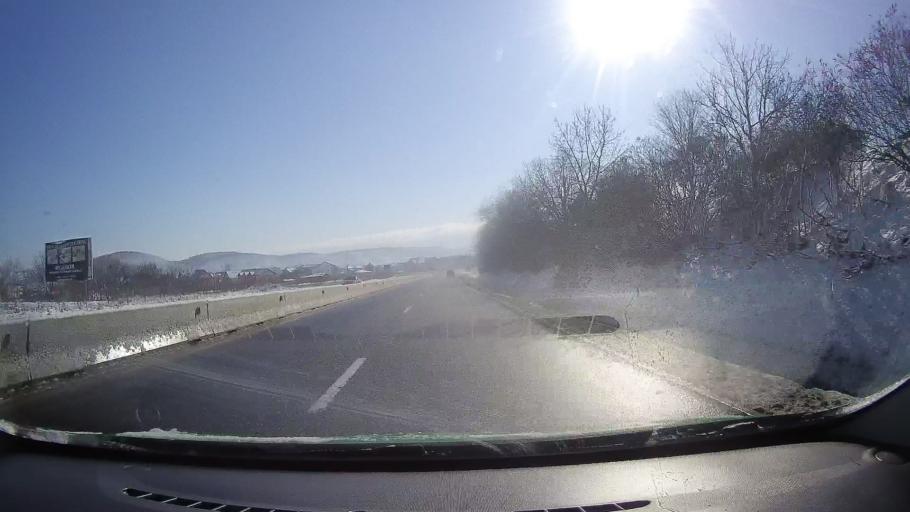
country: RO
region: Sibiu
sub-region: Comuna Selimbar
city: Selimbar
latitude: 45.7598
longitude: 24.1960
